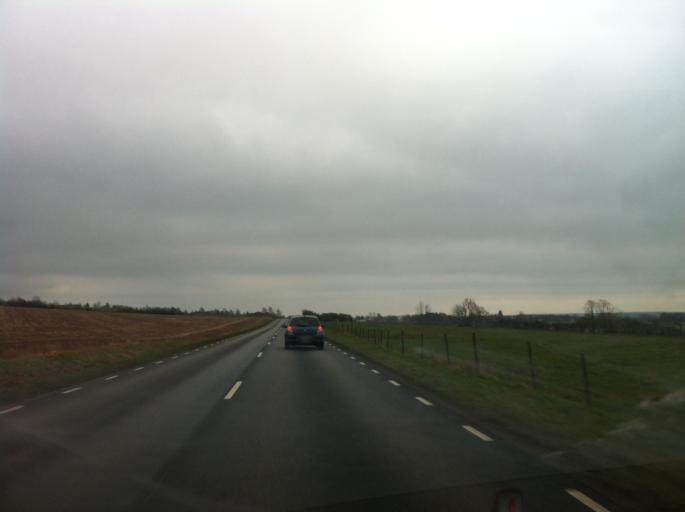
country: SE
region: Skane
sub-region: Hoors Kommun
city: Loberod
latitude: 55.7230
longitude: 13.5075
